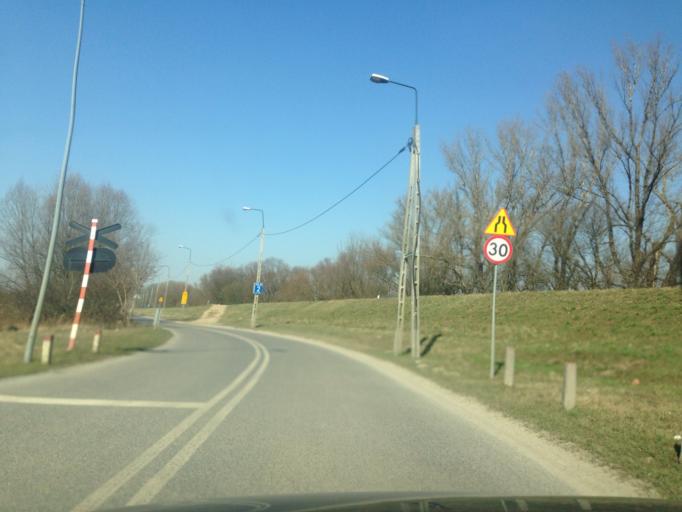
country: PL
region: Masovian Voivodeship
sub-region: Warszawa
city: Wilanow
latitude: 52.1813
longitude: 21.1122
